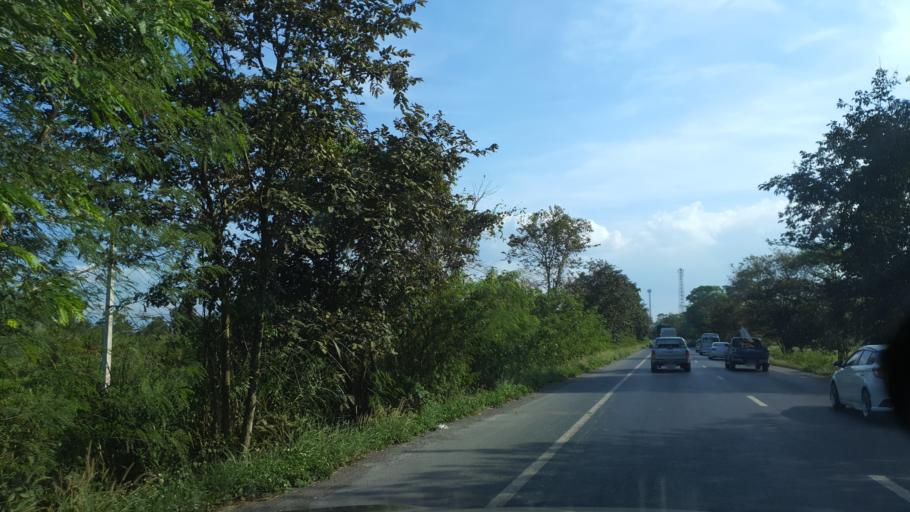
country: TH
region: Surat Thani
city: Ban Na Doem
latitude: 8.9756
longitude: 99.2249
